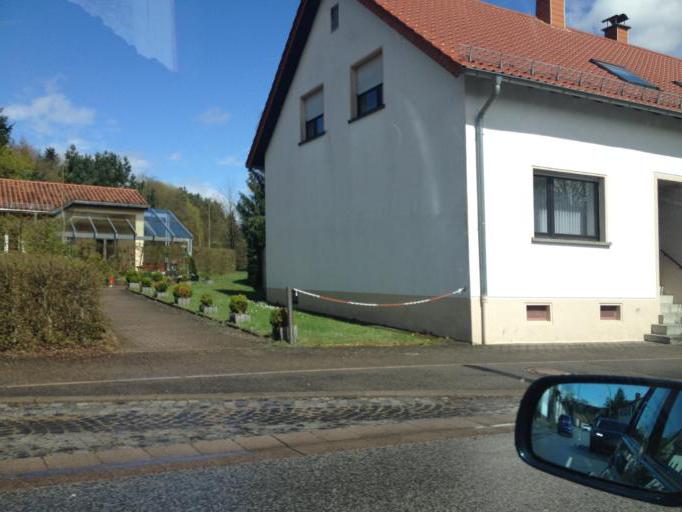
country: DE
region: Saarland
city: Bexbach
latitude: 49.3151
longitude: 7.2481
